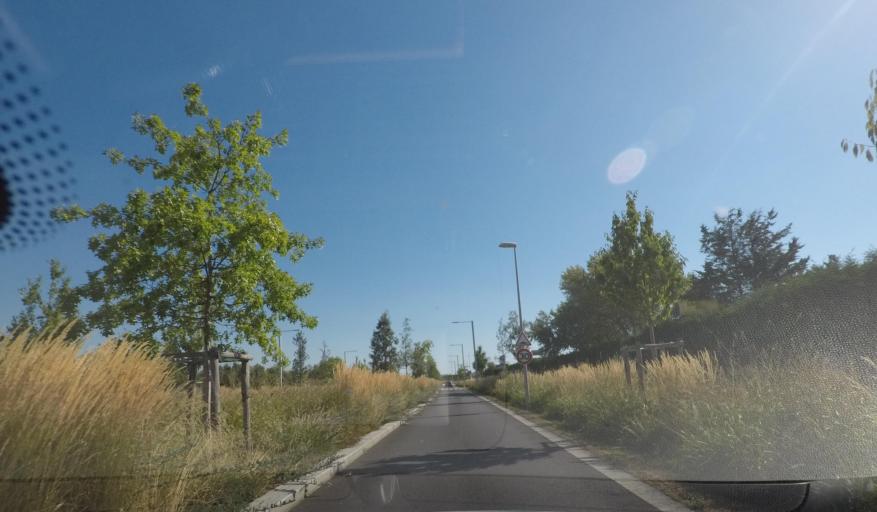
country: FR
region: Pays de la Loire
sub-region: Departement de la Loire-Atlantique
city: Saint-Nazaire
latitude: 47.3011
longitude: -2.2070
